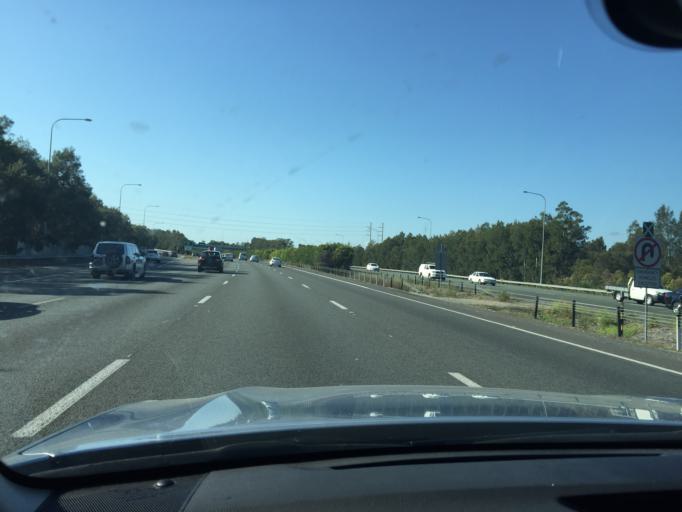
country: AU
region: Queensland
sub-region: Gold Coast
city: Yatala
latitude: -27.7163
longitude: 153.2100
